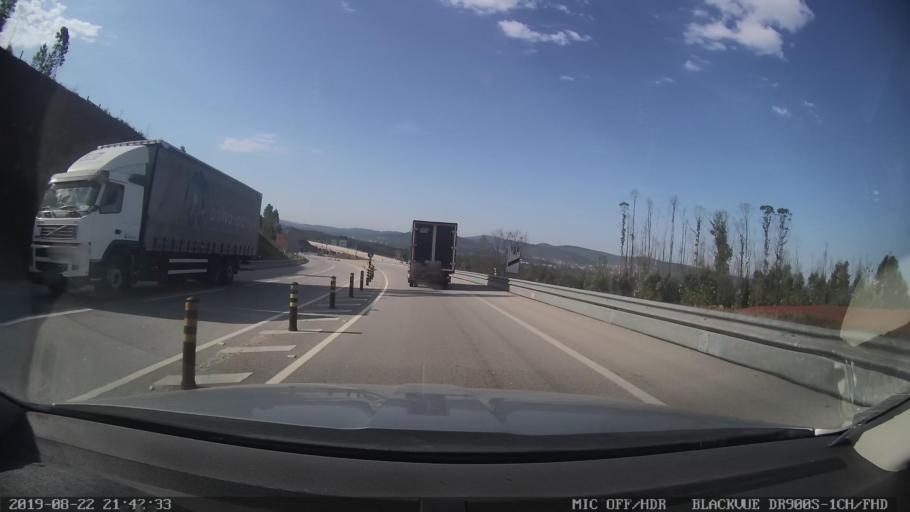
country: PT
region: Leiria
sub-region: Figueiro Dos Vinhos
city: Figueiro dos Vinhos
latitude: 39.9295
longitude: -8.3422
